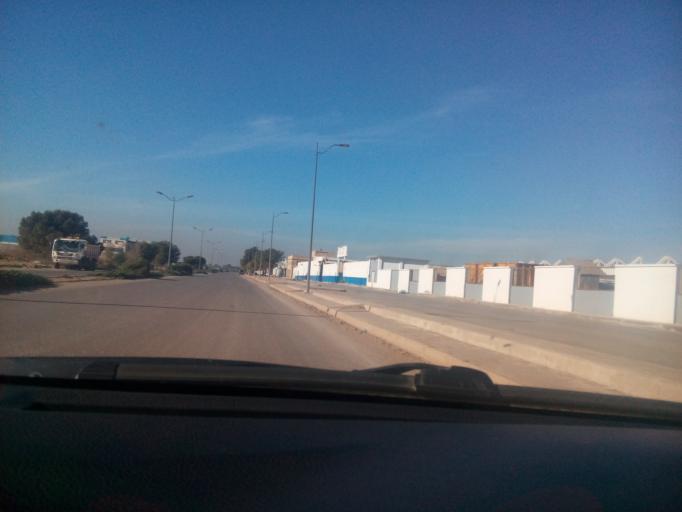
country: DZ
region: Oran
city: Es Senia
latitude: 35.6273
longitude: -0.5950
